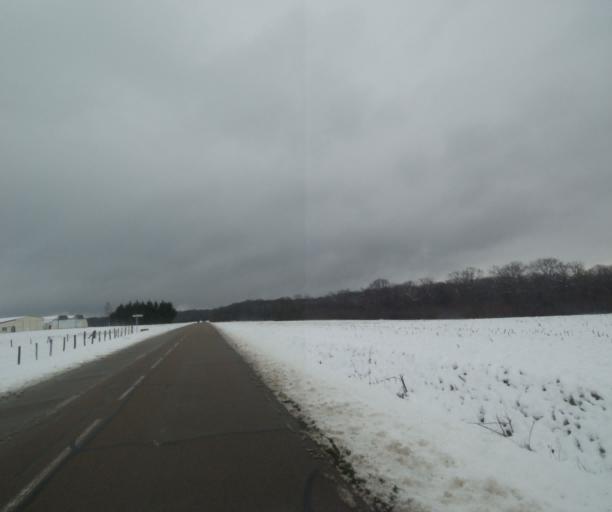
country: FR
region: Champagne-Ardenne
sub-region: Departement de la Haute-Marne
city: Laneuville-a-Remy
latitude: 48.4333
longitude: 4.8548
